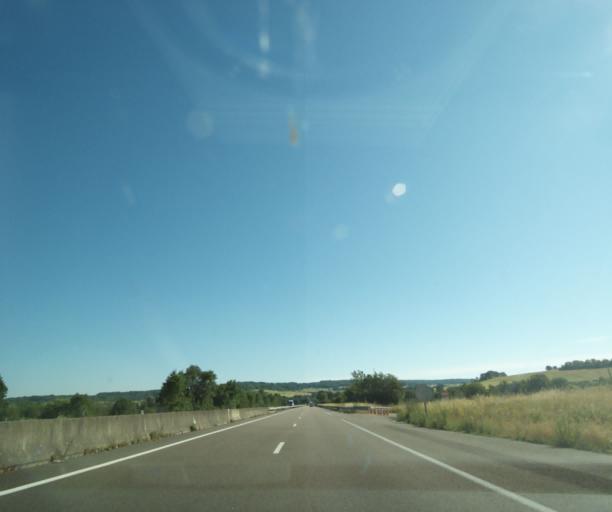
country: FR
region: Champagne-Ardenne
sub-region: Departement de la Haute-Marne
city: Rolampont
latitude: 47.9341
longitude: 5.2910
